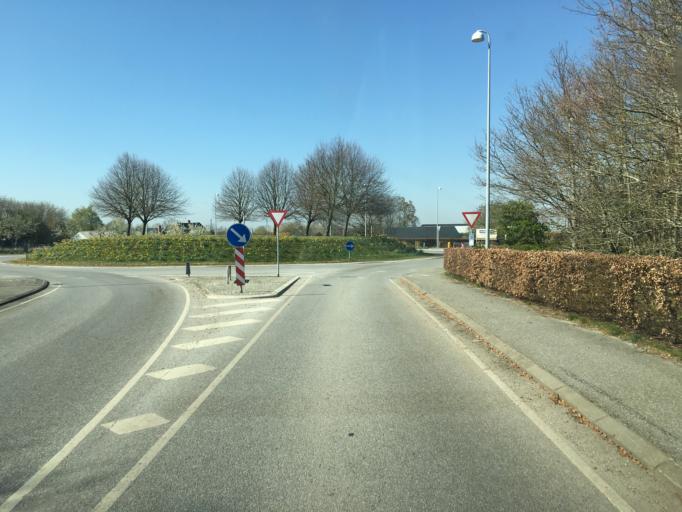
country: DK
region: South Denmark
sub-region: Aabenraa Kommune
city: Rodekro
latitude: 55.0209
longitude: 9.3204
